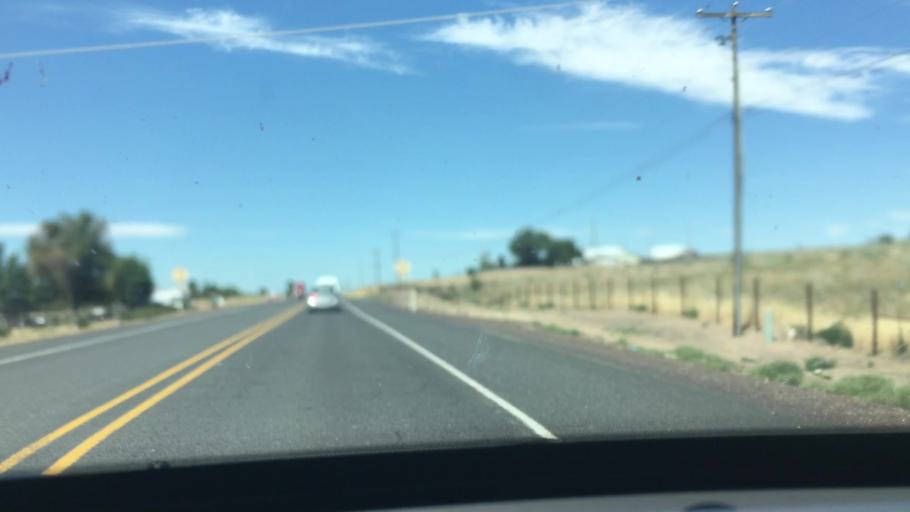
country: US
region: Oregon
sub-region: Jefferson County
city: Madras
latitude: 44.5727
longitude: -121.1593
